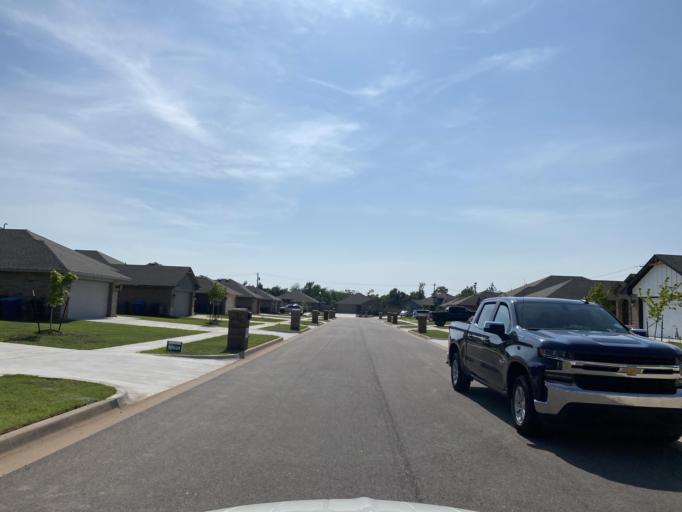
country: US
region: Oklahoma
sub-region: Oklahoma County
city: Nicoma Park
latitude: 35.4422
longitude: -97.3429
